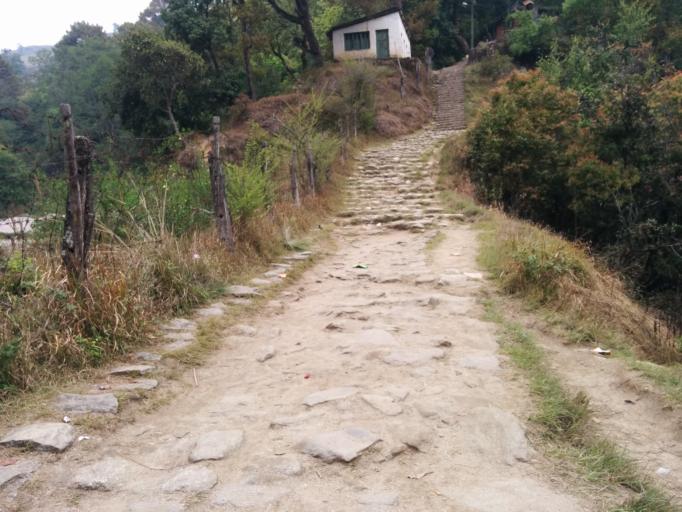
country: NP
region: Central Region
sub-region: Bagmati Zone
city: Bhaktapur
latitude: 27.7718
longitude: 85.4261
